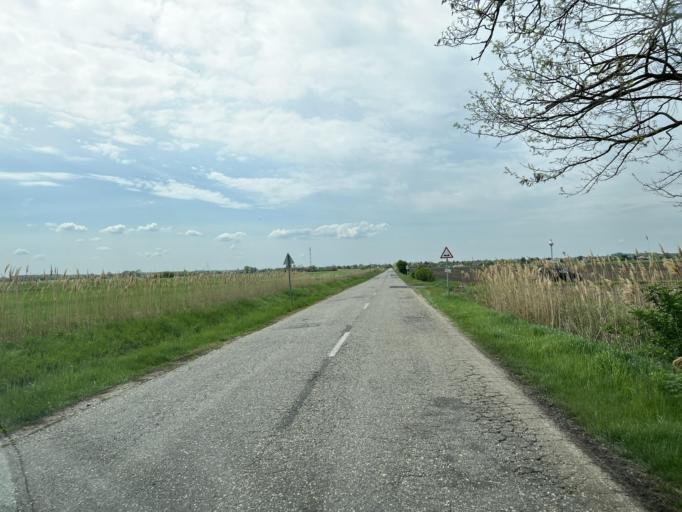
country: HU
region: Pest
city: Tortel
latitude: 47.1334
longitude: 19.9496
